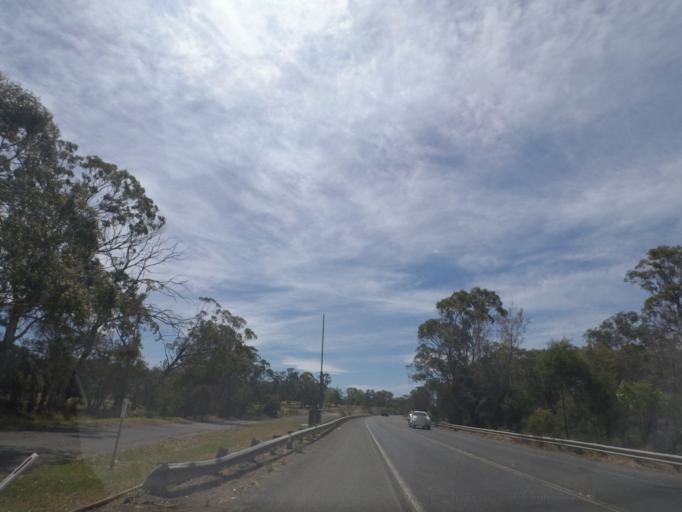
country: AU
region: New South Wales
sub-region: Wollondilly
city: Buxton
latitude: -34.2687
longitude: 150.5740
